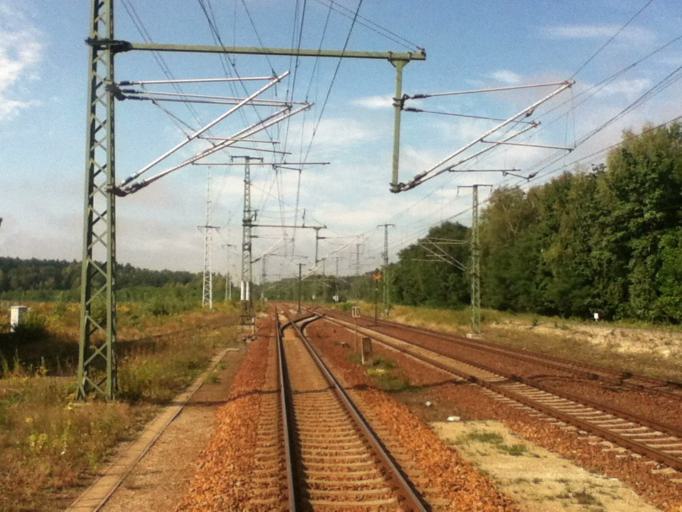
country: DE
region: Brandenburg
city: Senftenberg
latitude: 51.5072
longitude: 13.9546
